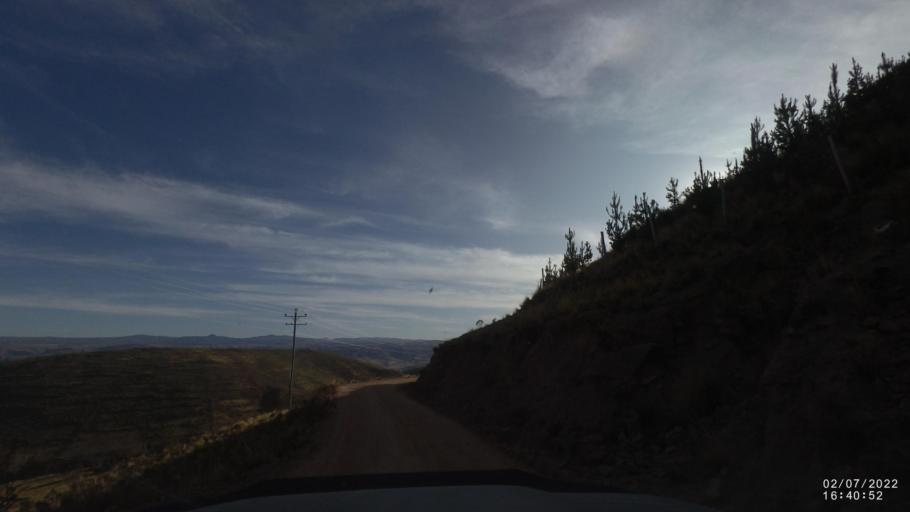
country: BO
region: Cochabamba
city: Irpa Irpa
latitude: -17.9727
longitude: -66.4987
